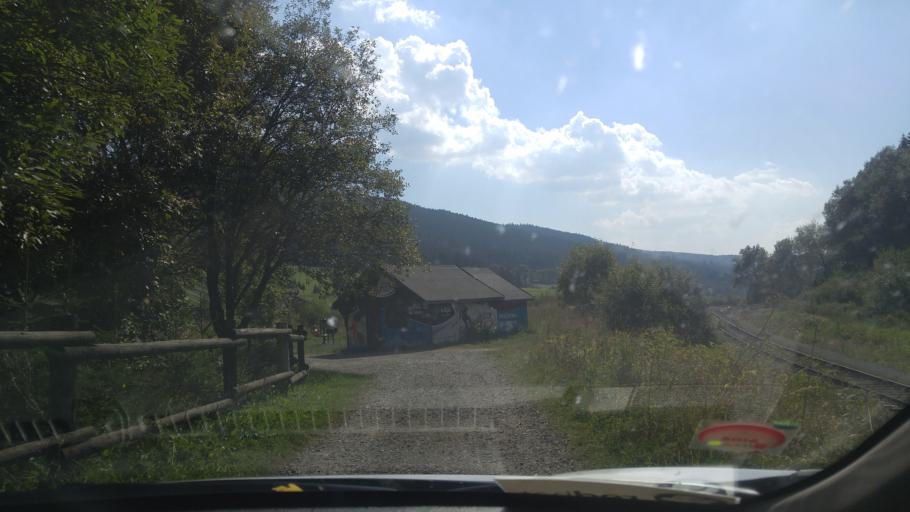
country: CZ
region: Olomoucky
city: Vapenna
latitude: 50.1934
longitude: 17.0638
